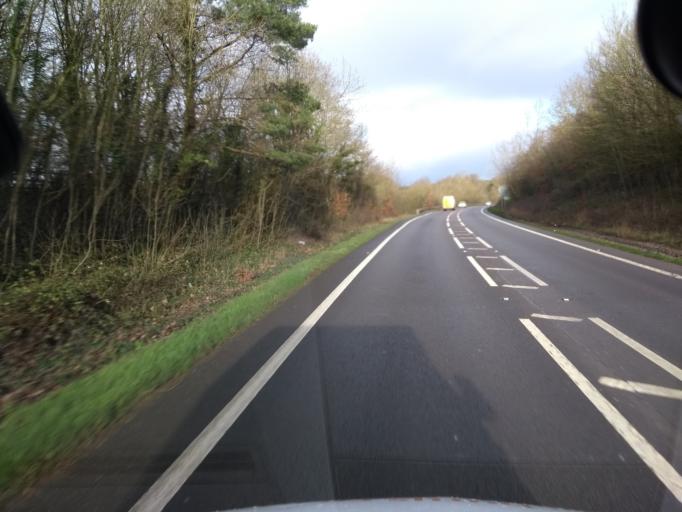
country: GB
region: England
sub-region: Somerset
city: Creech Saint Michael
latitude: 50.9752
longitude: -3.0088
